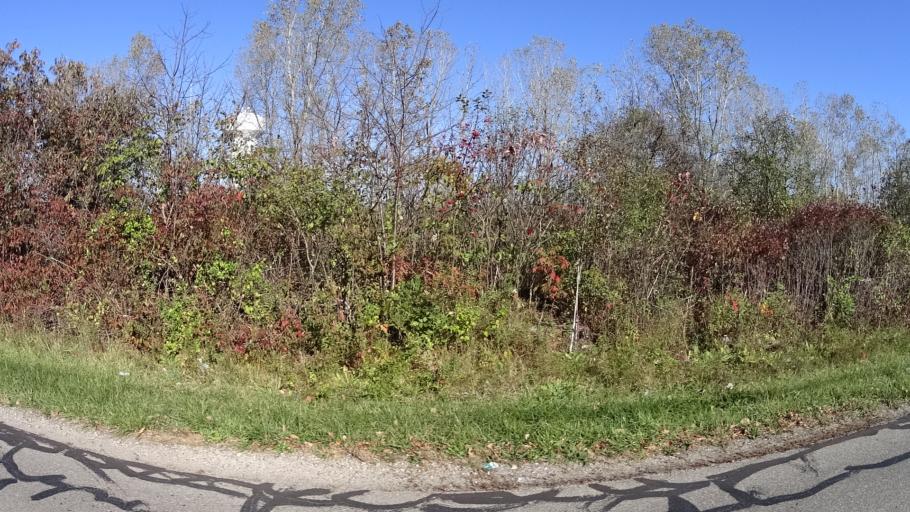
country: US
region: Ohio
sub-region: Lorain County
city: Lorain
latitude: 41.4362
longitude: -82.1484
